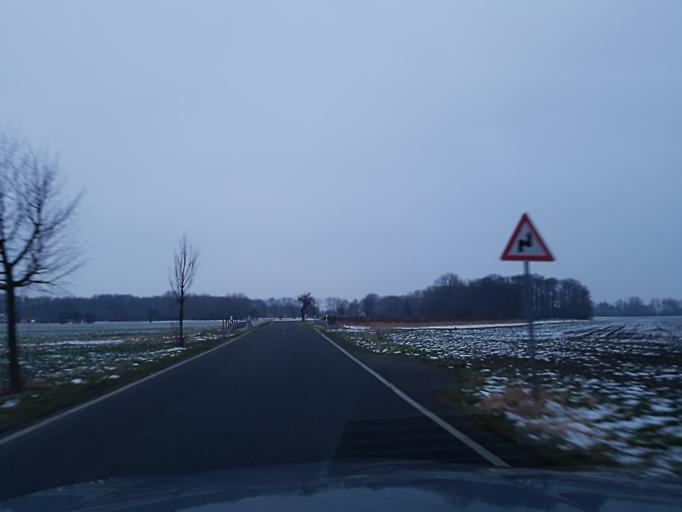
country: DE
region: Saxony
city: Stauchitz
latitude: 51.2531
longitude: 13.2078
